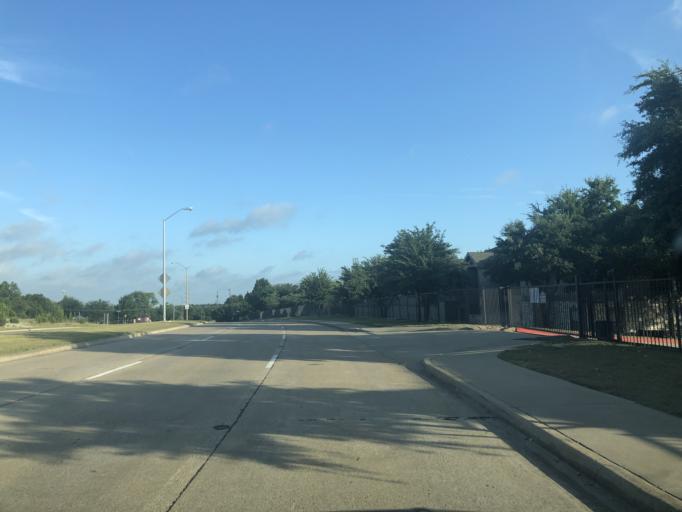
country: US
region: Texas
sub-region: Dallas County
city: Duncanville
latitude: 32.6658
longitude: -96.9437
